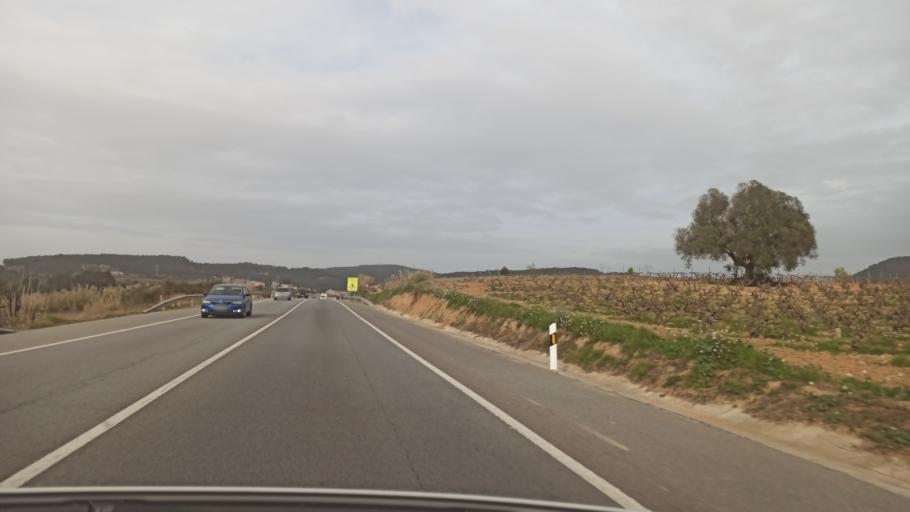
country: ES
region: Catalonia
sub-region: Provincia de Barcelona
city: Avinyonet del Penedes
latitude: 41.3745
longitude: 1.8061
